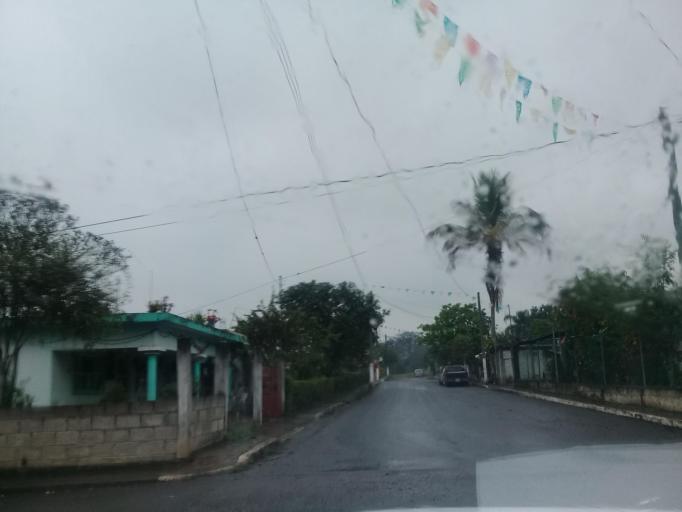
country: MX
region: Veracruz
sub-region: Cordoba
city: San Jose de Tapia
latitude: 18.8448
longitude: -96.9578
